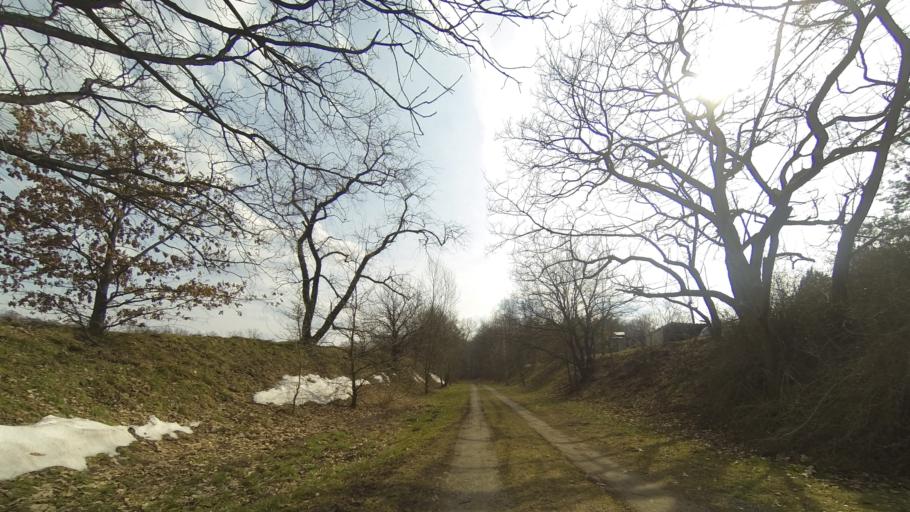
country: DE
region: Saxony
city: Radeburg
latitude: 51.2339
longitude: 13.7061
